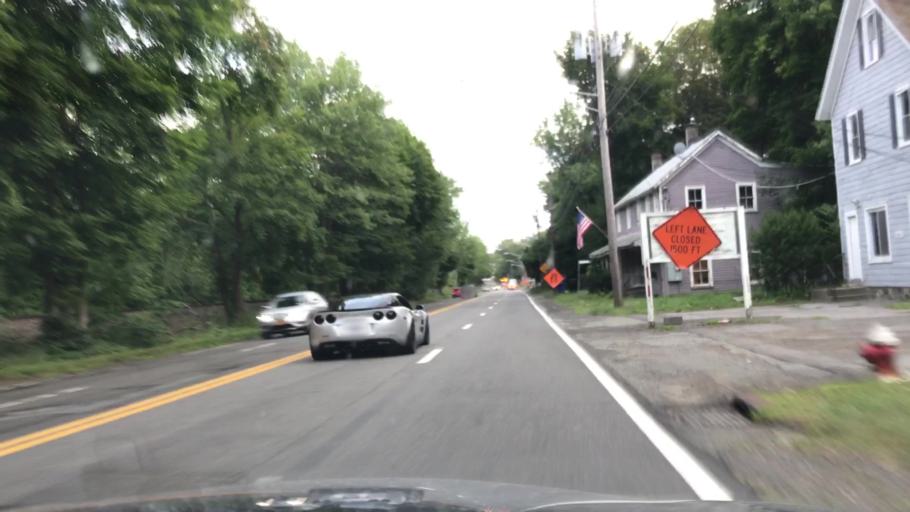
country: US
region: New York
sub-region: Rockland County
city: Sloatsburg
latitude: 41.1736
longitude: -74.1890
